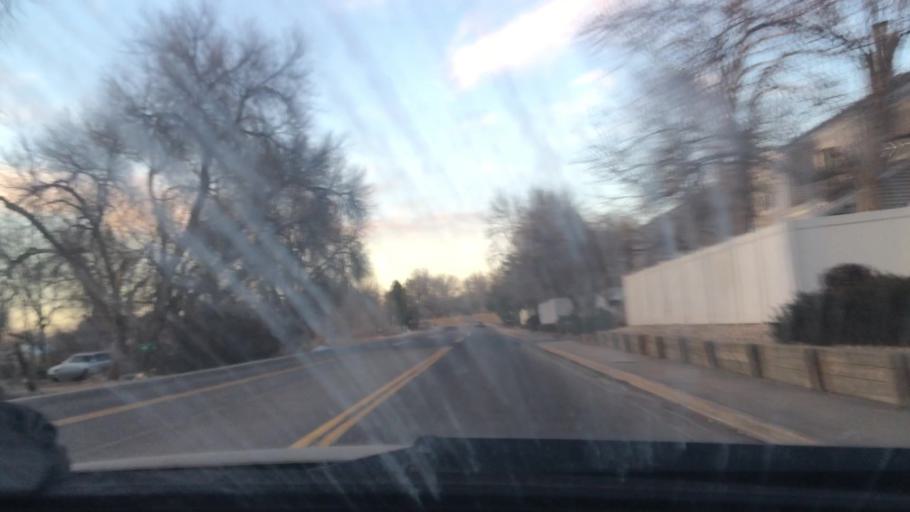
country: US
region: Colorado
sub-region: Arapahoe County
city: Glendale
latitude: 39.6756
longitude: -104.8845
